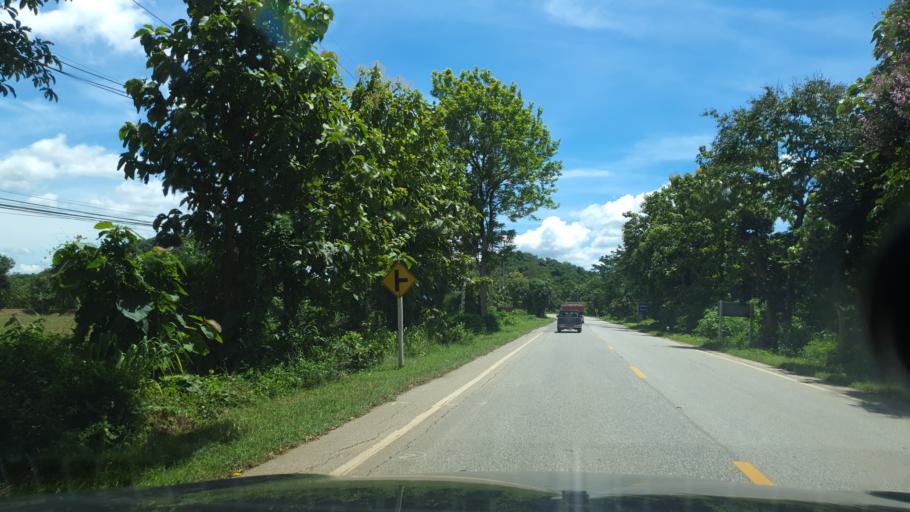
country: TH
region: Sukhothai
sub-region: Amphoe Si Satchanalai
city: Si Satchanalai
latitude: 17.4440
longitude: 99.7936
